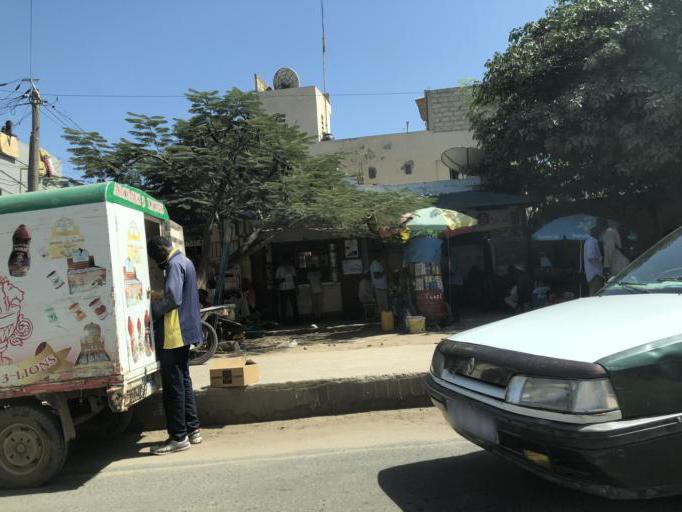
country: SN
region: Dakar
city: Mermoz Boabab
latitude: 14.7259
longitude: -17.4883
